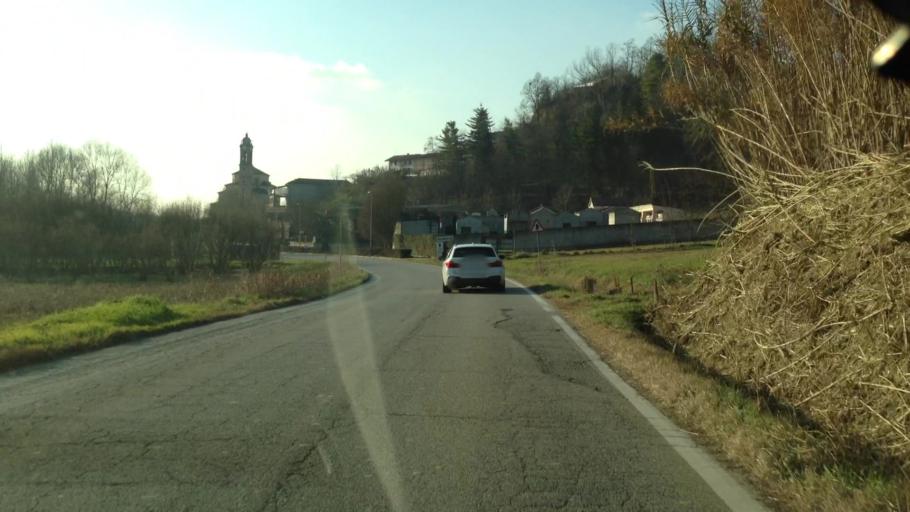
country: IT
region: Piedmont
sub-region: Provincia di Asti
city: Belveglio
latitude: 44.8308
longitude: 8.3358
